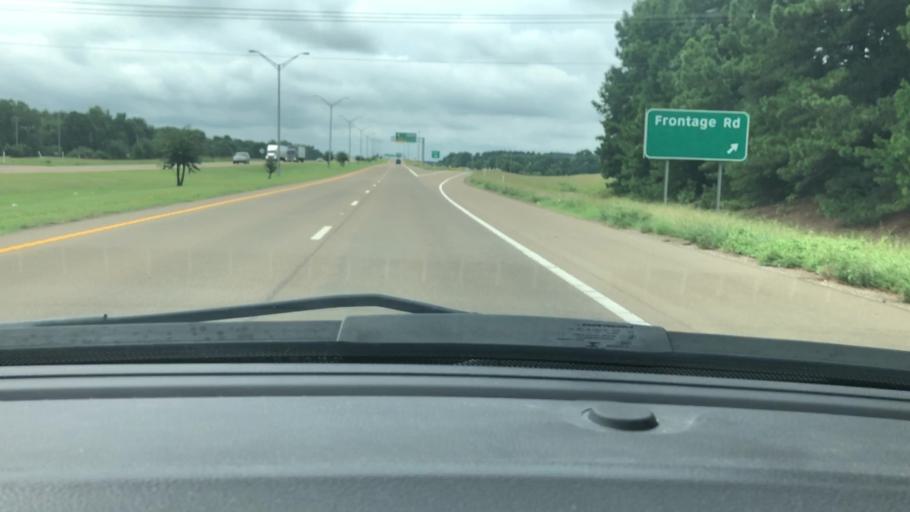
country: US
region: Texas
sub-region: Bowie County
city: Wake Village
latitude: 33.4097
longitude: -94.0976
